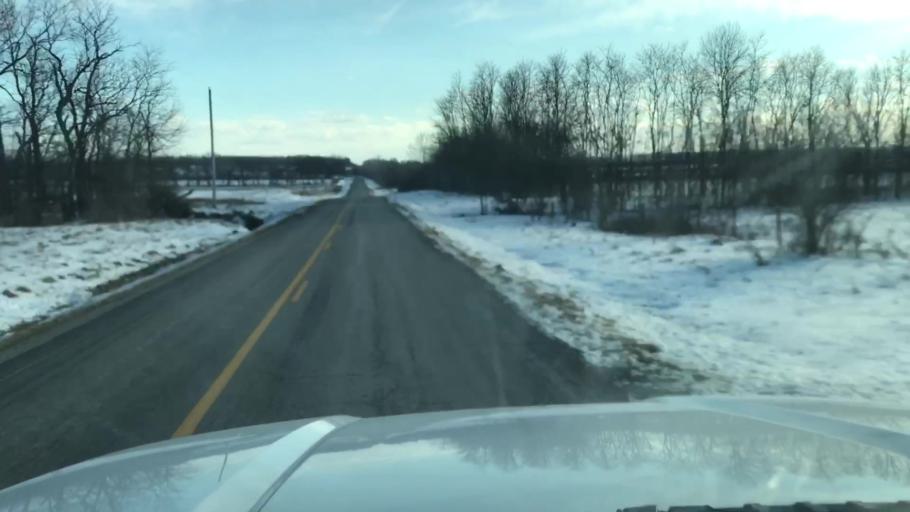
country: US
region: Missouri
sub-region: Holt County
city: Oregon
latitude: 40.1104
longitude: -95.0226
